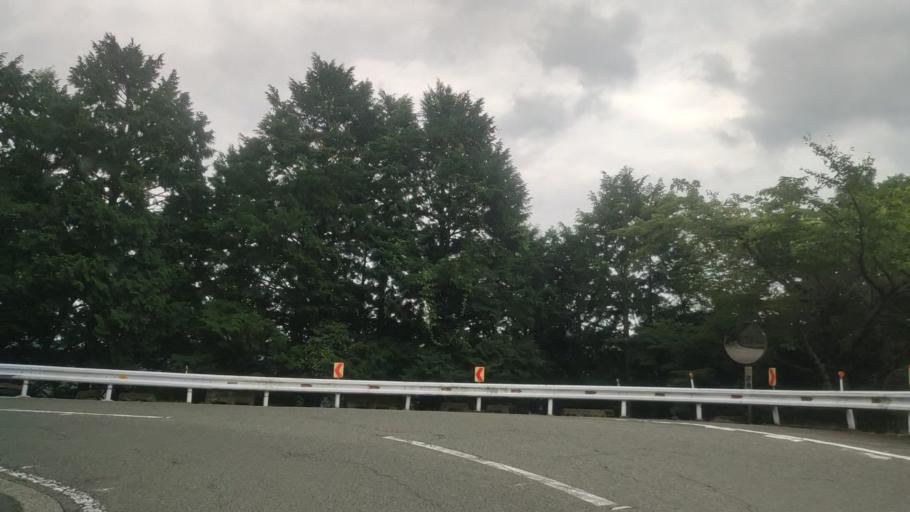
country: JP
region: Wakayama
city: Koya
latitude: 34.2108
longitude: 135.5421
